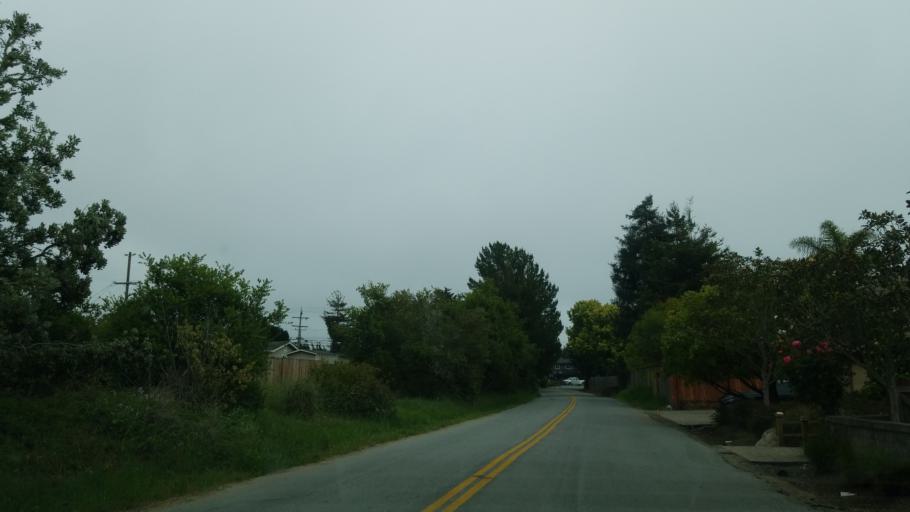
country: US
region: California
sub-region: Santa Cruz County
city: Seacliff
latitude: 36.9776
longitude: -121.9183
